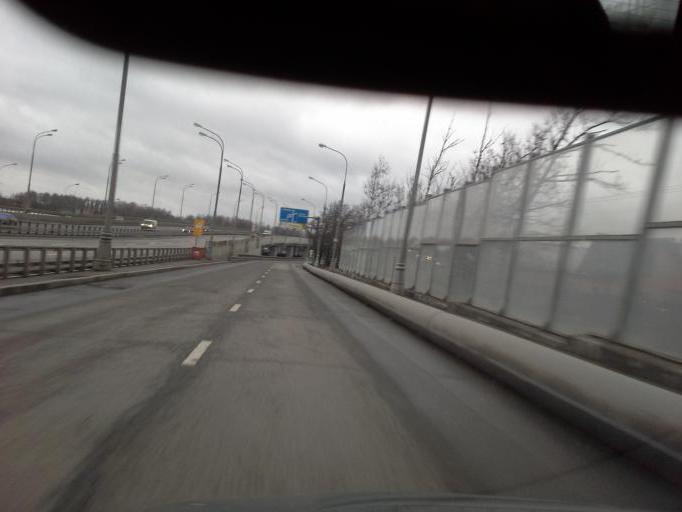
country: RU
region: Moscow
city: Vnukovo
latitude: 55.5951
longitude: 37.2383
